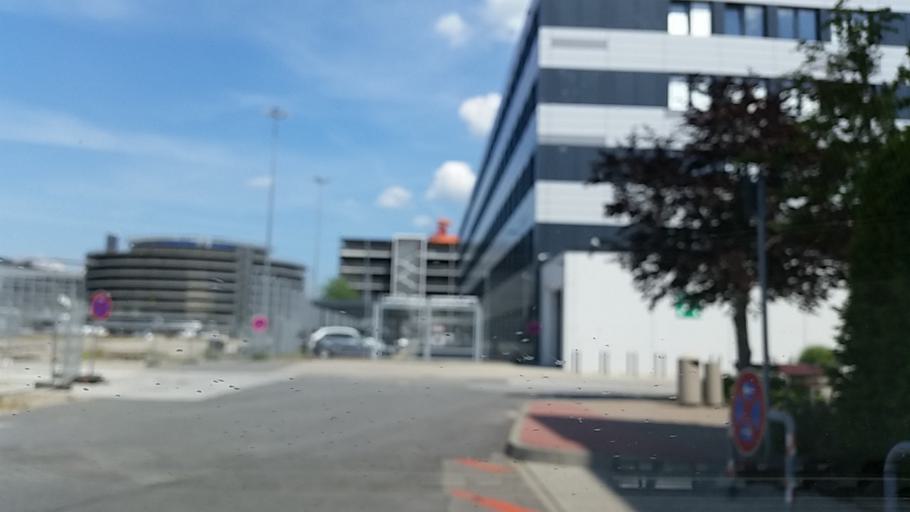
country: DE
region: Hamburg
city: Fuhlsbuettel
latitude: 53.6280
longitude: 10.0055
